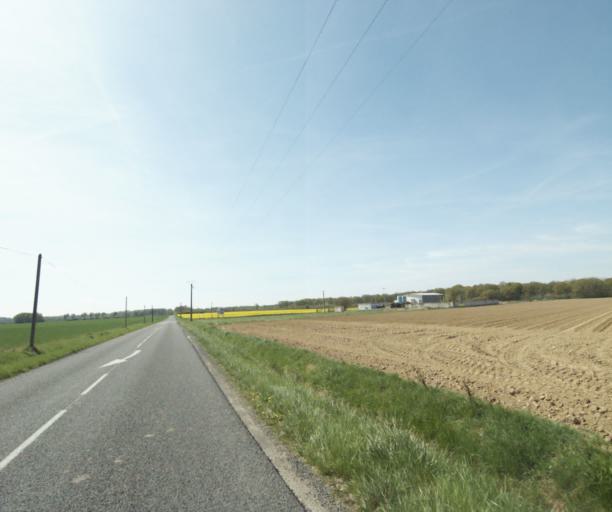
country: FR
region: Ile-de-France
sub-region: Departement de Seine-et-Marne
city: Nangis
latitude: 48.5486
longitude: 2.9985
